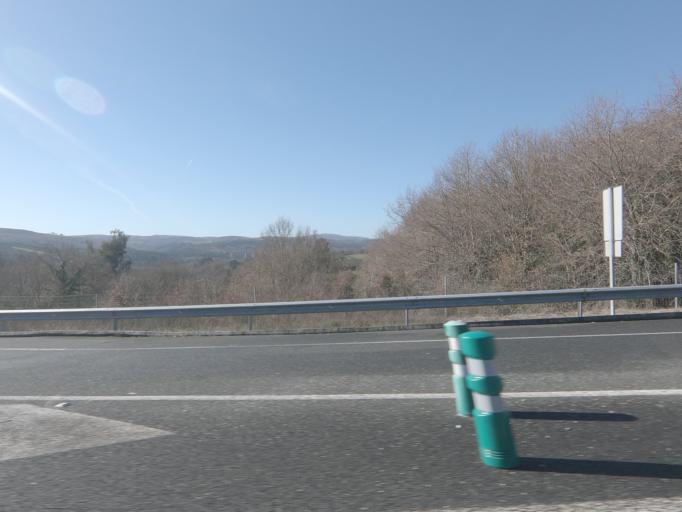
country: ES
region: Galicia
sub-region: Provincia de Pontevedra
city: Lalin
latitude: 42.6225
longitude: -8.1008
